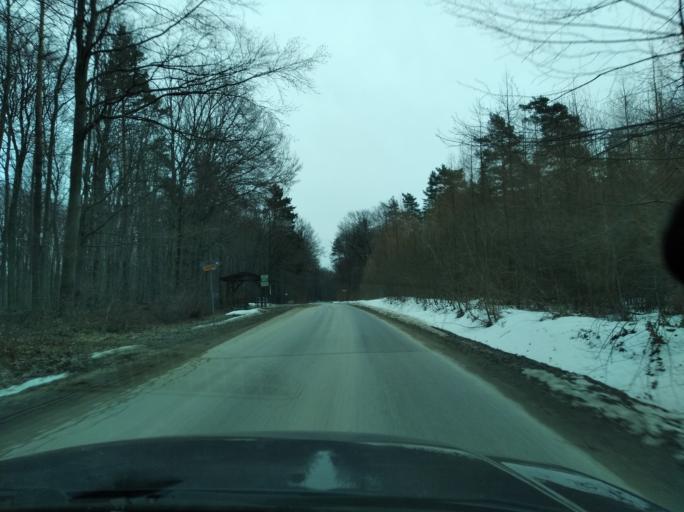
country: PL
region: Subcarpathian Voivodeship
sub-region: Powiat rzeszowski
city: Straszydle
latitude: 49.9320
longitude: 21.9927
